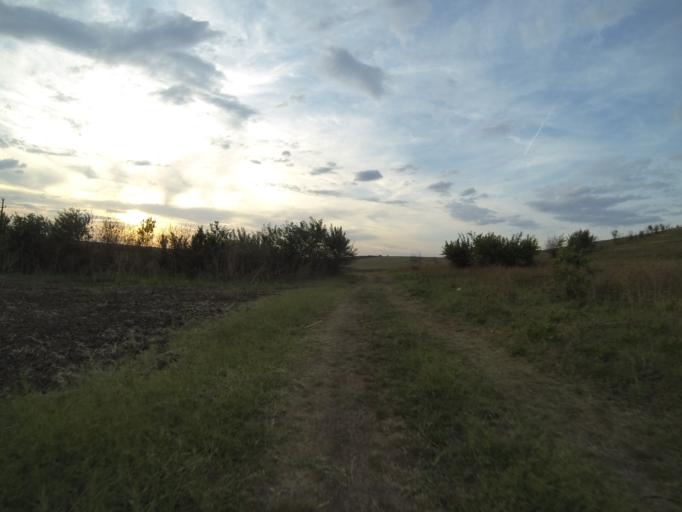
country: RO
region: Dolj
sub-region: Comuna Ceratu
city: Ceratu
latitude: 44.0933
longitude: 23.6670
